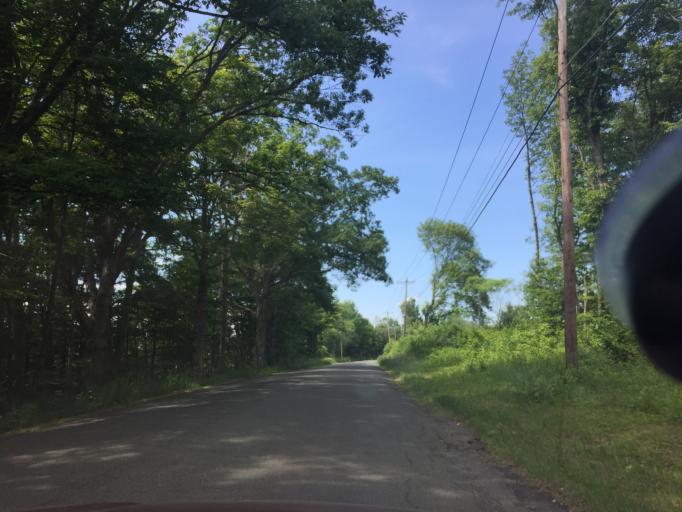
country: US
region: Connecticut
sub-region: Litchfield County
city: Litchfield
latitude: 41.8096
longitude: -73.2608
